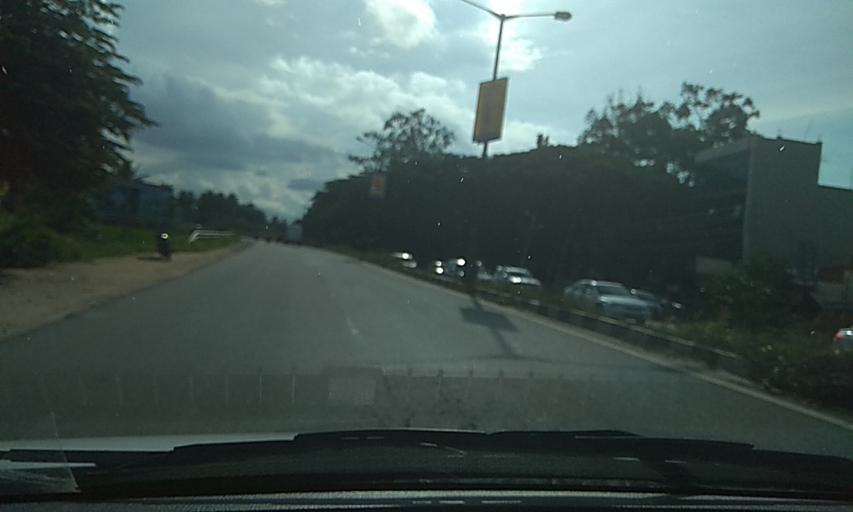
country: IN
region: Karnataka
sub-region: Mandya
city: Shrirangapattana
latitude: 12.4178
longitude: 76.6755
